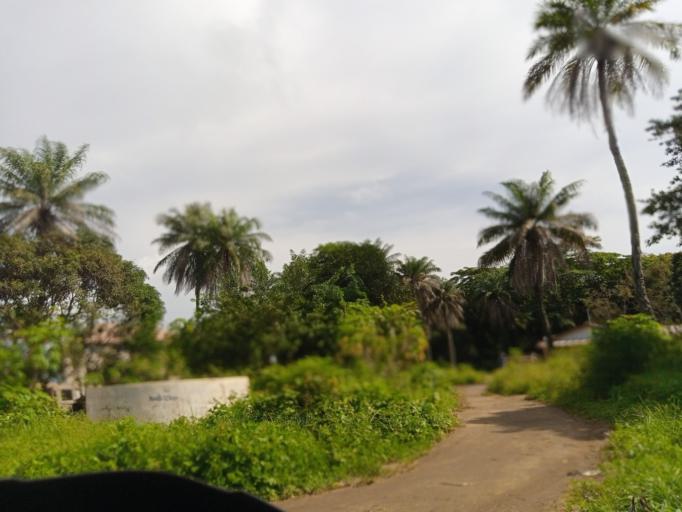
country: SL
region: Northern Province
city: Masoyila
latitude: 8.6094
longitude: -13.2039
